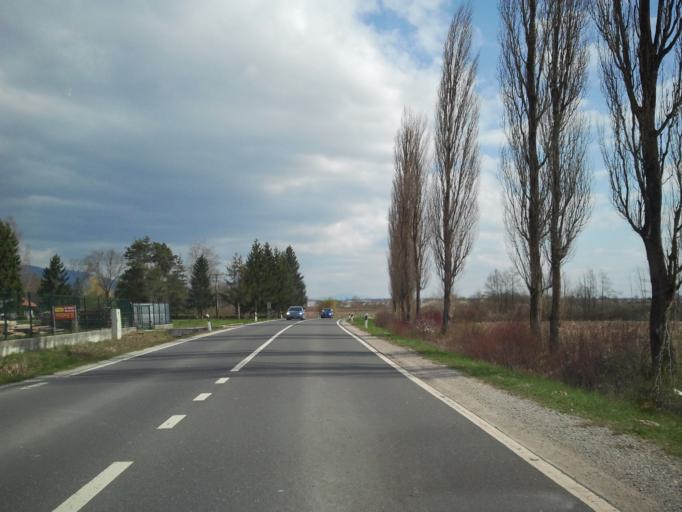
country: HR
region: Zagrebacka
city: Jastrebarsko
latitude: 45.6502
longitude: 15.6278
